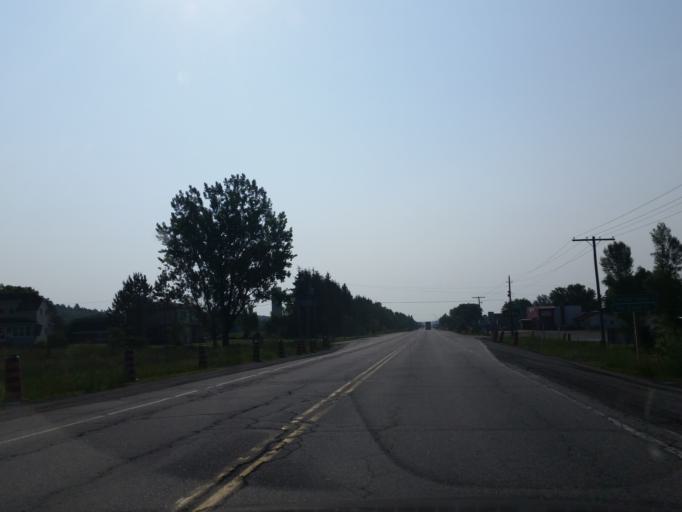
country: CA
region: Ontario
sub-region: Nipissing District
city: North Bay
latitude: 46.4139
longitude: -80.1306
